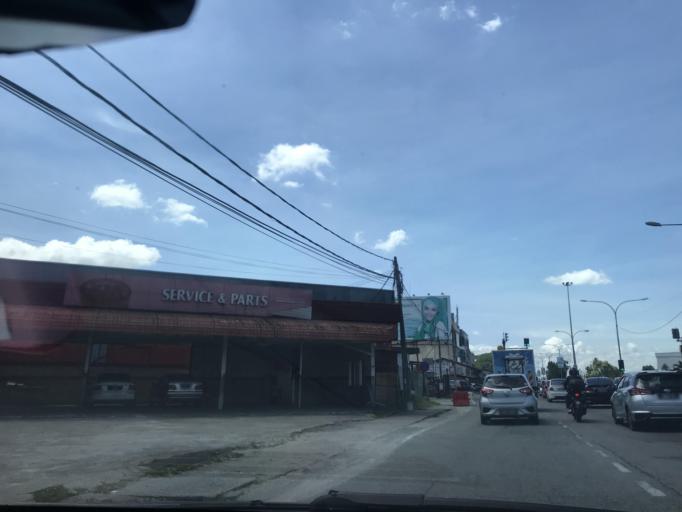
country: MY
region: Kelantan
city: Kota Bharu
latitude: 6.1035
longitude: 102.2621
